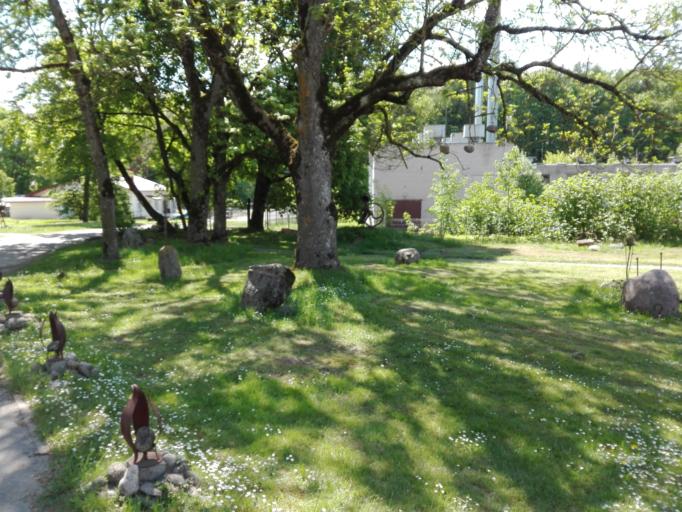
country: LT
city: Grigiskes
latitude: 54.6302
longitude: 25.1058
